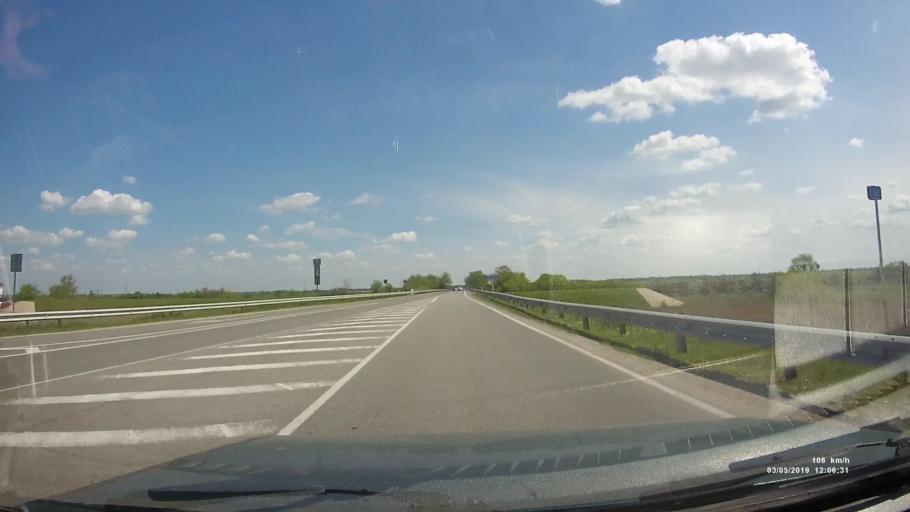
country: RU
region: Rostov
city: Bagayevskaya
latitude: 47.2854
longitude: 40.4539
